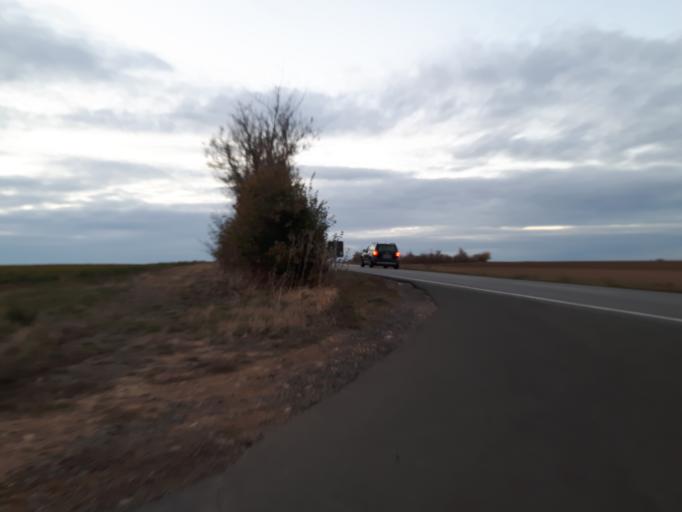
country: DE
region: Rheinland-Pfalz
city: Gundersheim
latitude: 49.6719
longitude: 8.1883
